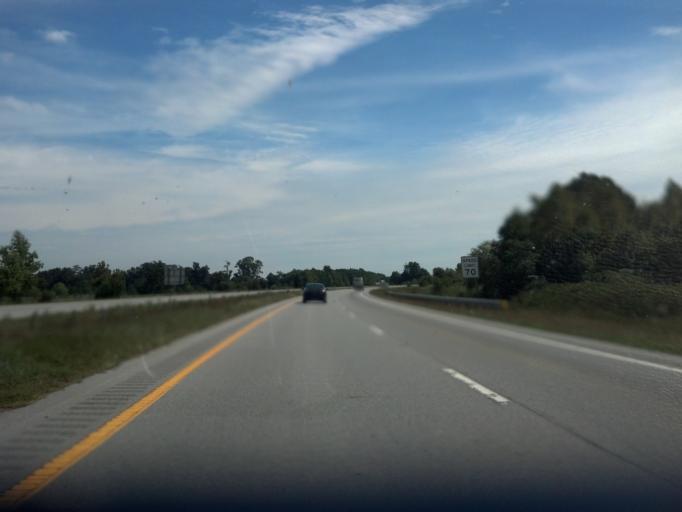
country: US
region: North Carolina
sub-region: Pitt County
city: Greenville
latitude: 35.6653
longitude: -77.4005
